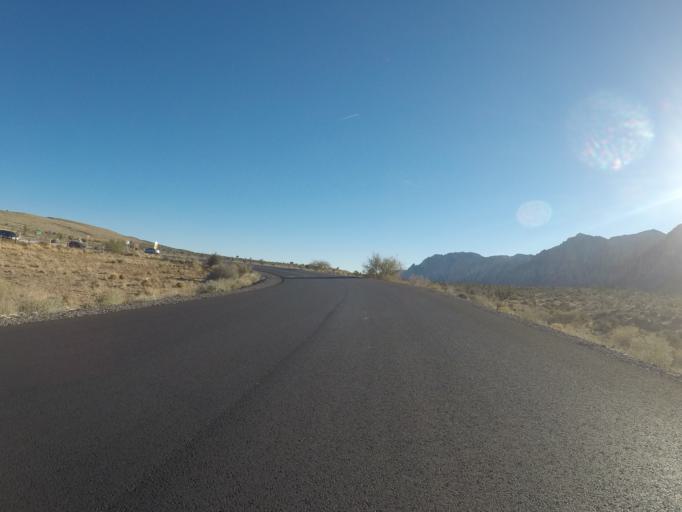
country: US
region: Nevada
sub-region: Clark County
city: Summerlin South
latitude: 36.1121
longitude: -115.4503
